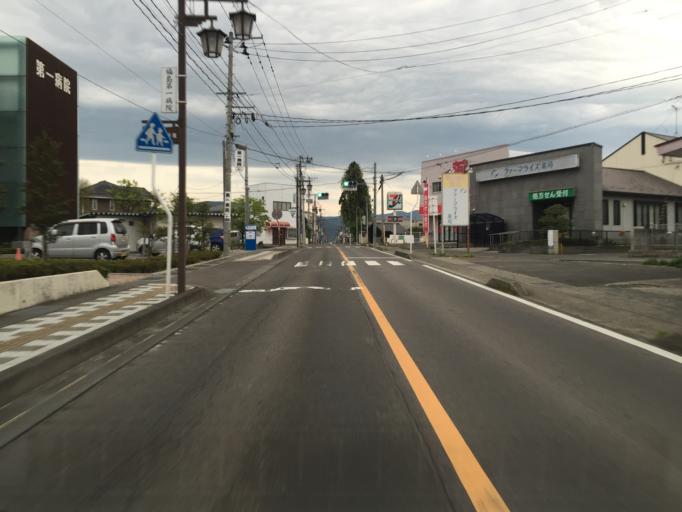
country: JP
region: Fukushima
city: Fukushima-shi
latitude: 37.7863
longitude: 140.4385
